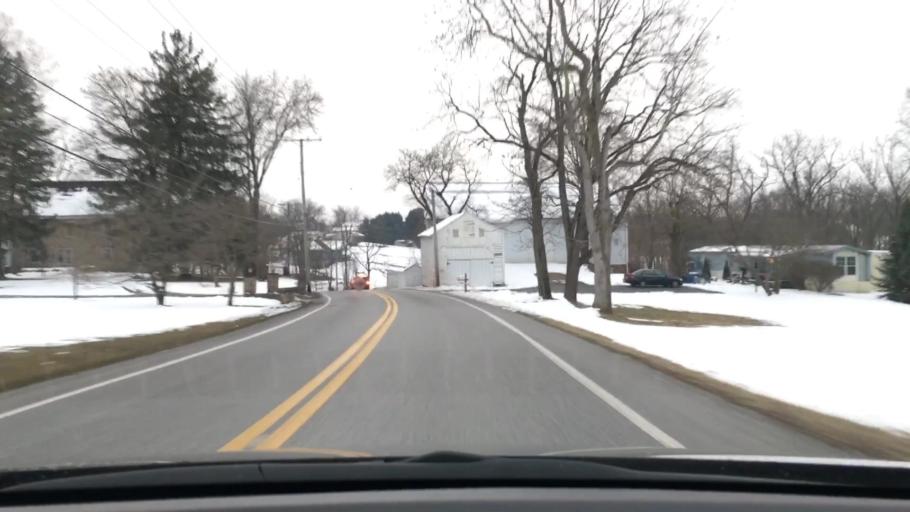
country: US
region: Pennsylvania
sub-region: York County
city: Weigelstown
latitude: 39.9599
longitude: -76.8374
